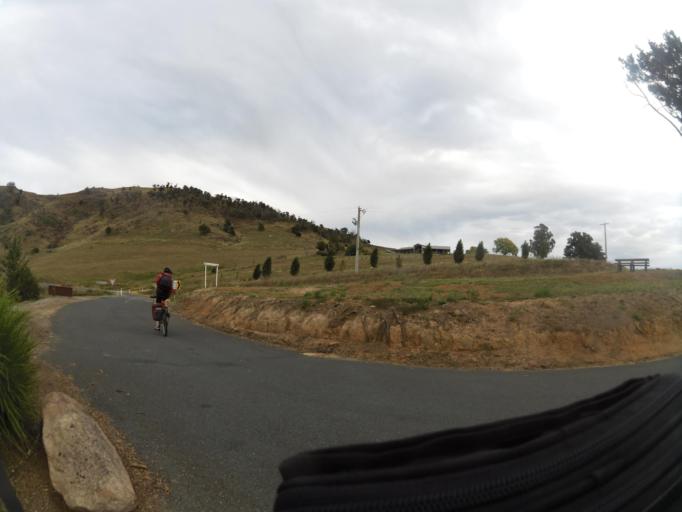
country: AU
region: New South Wales
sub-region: Snowy River
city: Jindabyne
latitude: -36.0856
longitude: 147.9780
